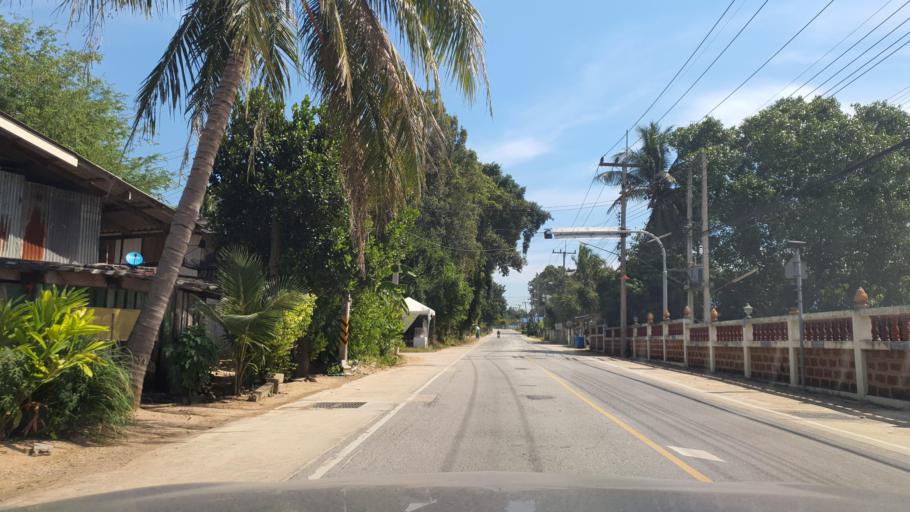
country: TH
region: Chon Buri
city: Bang Lamung
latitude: 12.9842
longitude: 100.9696
